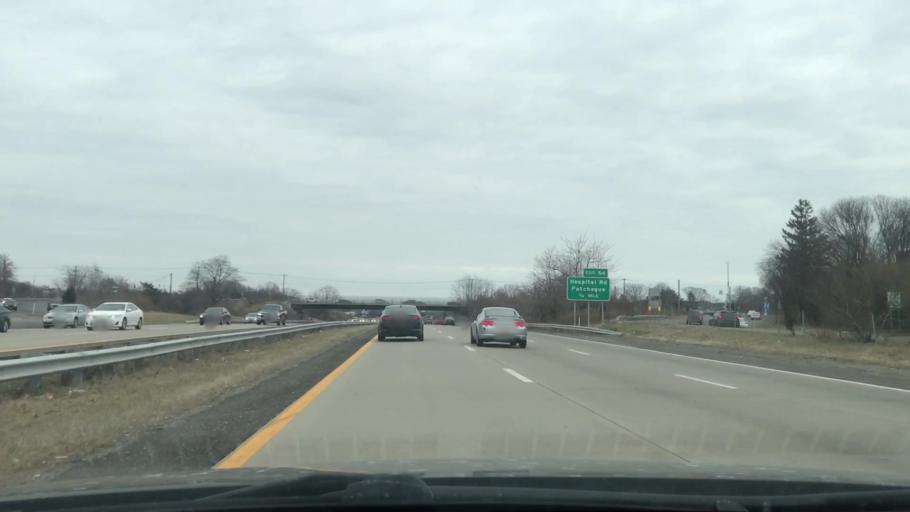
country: US
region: New York
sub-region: Suffolk County
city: North Patchogue
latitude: 40.7794
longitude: -73.0116
